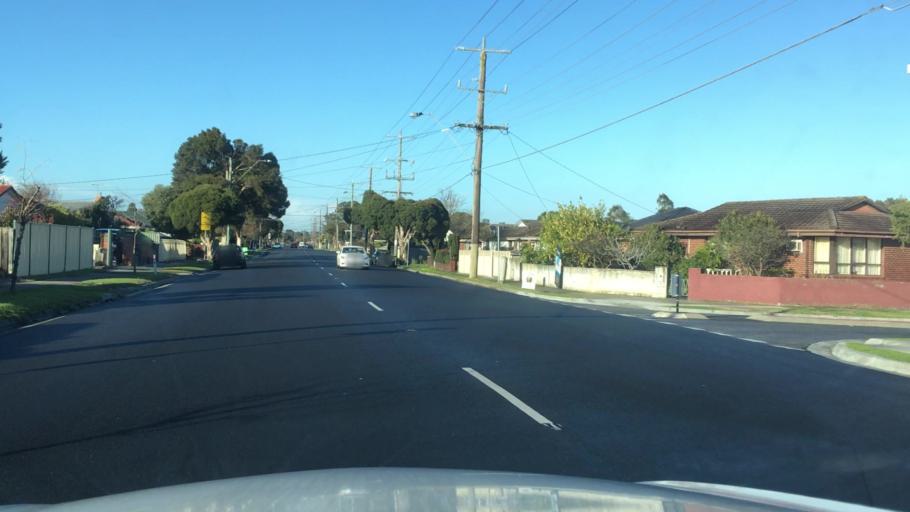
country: AU
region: Victoria
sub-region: Greater Dandenong
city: Keysborough
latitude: -37.9872
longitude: 145.1641
